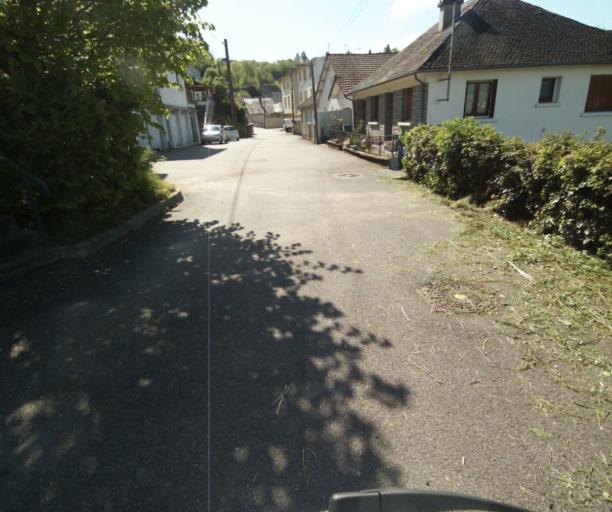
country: FR
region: Limousin
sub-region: Departement de la Correze
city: Tulle
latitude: 45.2696
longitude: 1.7779
